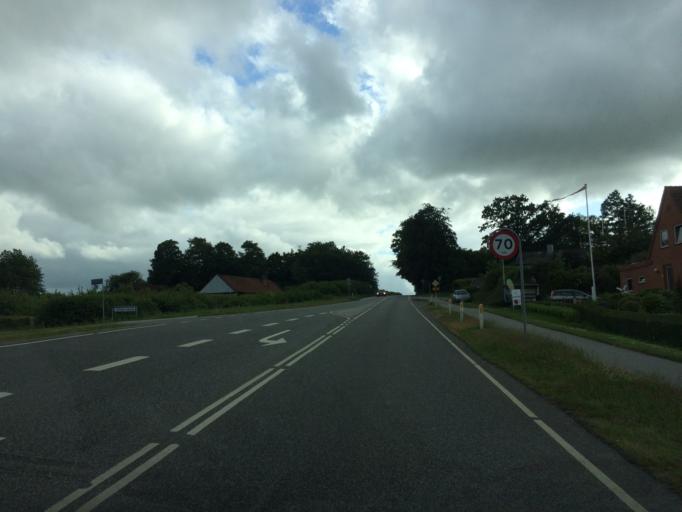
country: DK
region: South Denmark
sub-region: Sonderborg Kommune
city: Guderup
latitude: 54.9870
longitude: 9.9759
